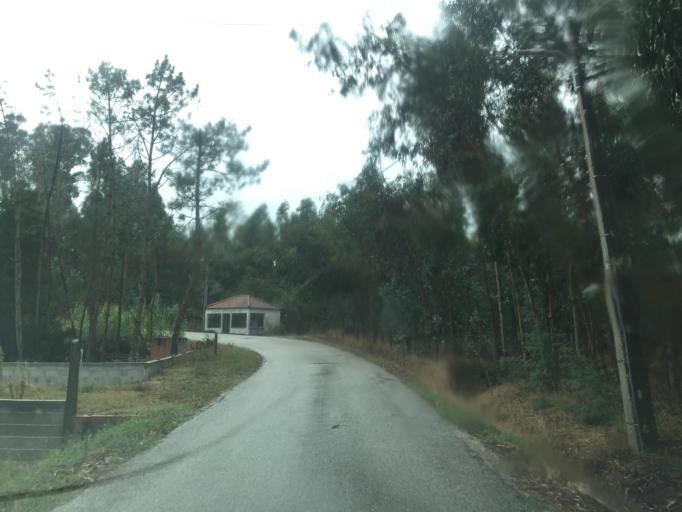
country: PT
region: Coimbra
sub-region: Figueira da Foz
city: Lavos
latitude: 40.0644
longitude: -8.7760
